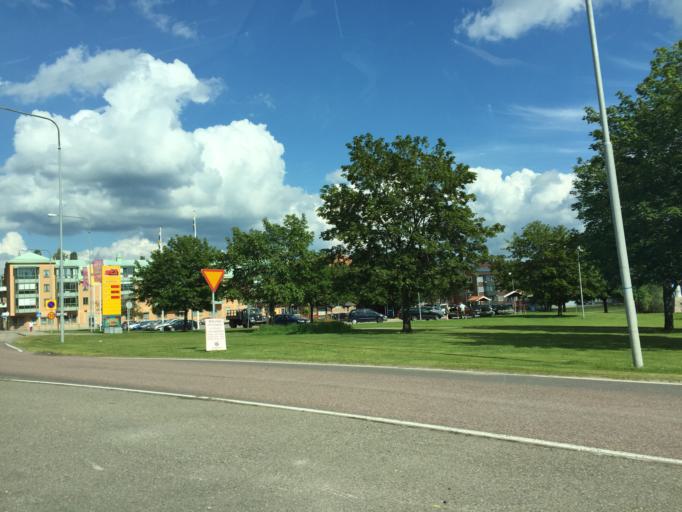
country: SE
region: Gaevleborg
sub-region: Bollnas Kommun
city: Bollnas
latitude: 61.3458
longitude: 16.3928
